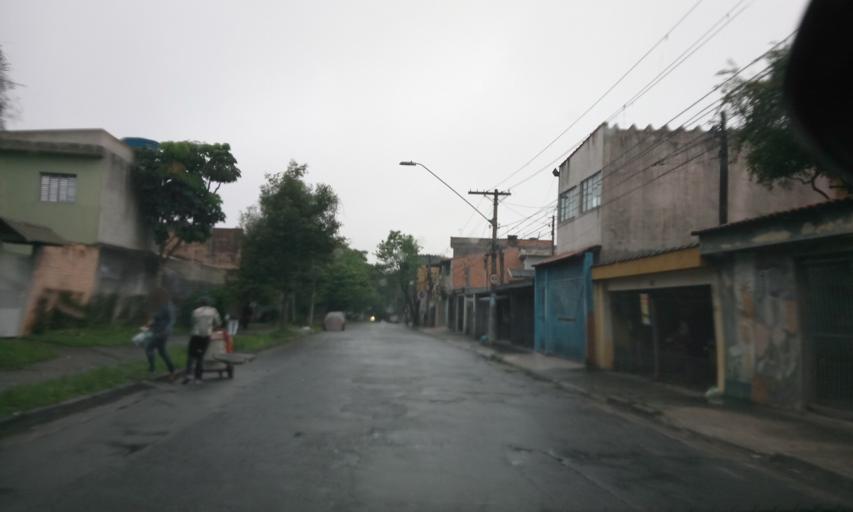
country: BR
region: Sao Paulo
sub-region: Santo Andre
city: Santo Andre
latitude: -23.7056
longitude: -46.5086
